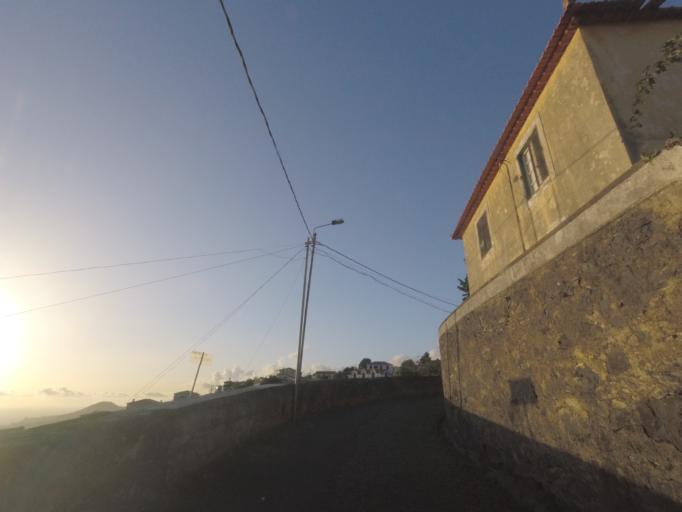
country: PT
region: Madeira
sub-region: Funchal
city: Nossa Senhora do Monte
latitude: 32.6541
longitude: -16.8818
